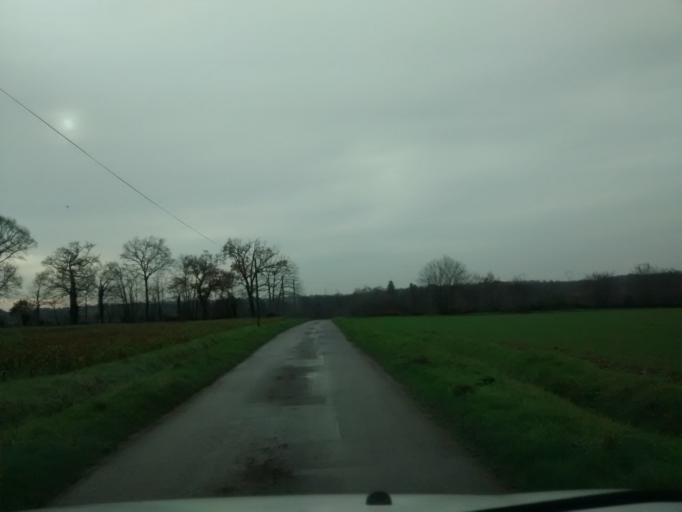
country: FR
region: Brittany
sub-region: Departement d'Ille-et-Vilaine
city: Acigne
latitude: 48.1302
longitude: -1.5540
